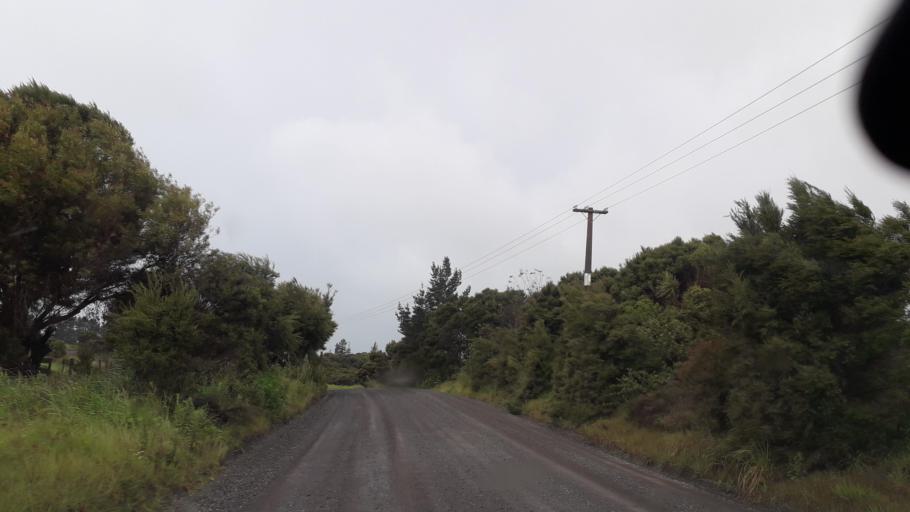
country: NZ
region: Northland
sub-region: Far North District
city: Kerikeri
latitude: -35.1372
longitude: 173.9981
